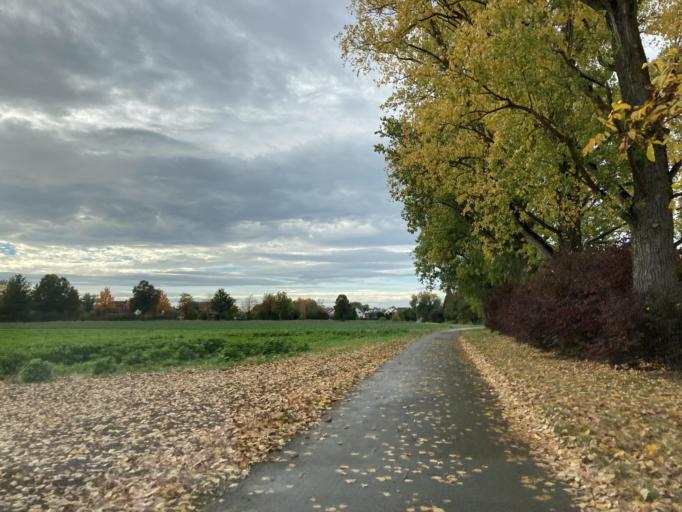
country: DE
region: Baden-Wuerttemberg
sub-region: Regierungsbezirk Stuttgart
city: Bondorf
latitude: 48.5077
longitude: 8.8871
